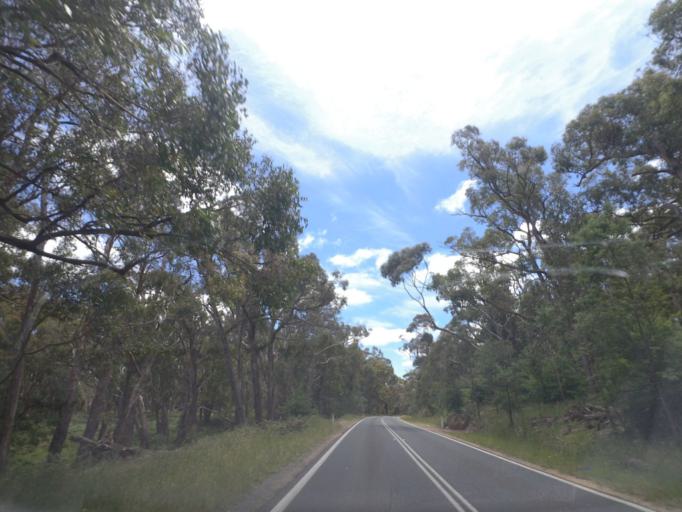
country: AU
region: Victoria
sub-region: Mount Alexander
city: Castlemaine
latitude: -37.3254
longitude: 144.1636
